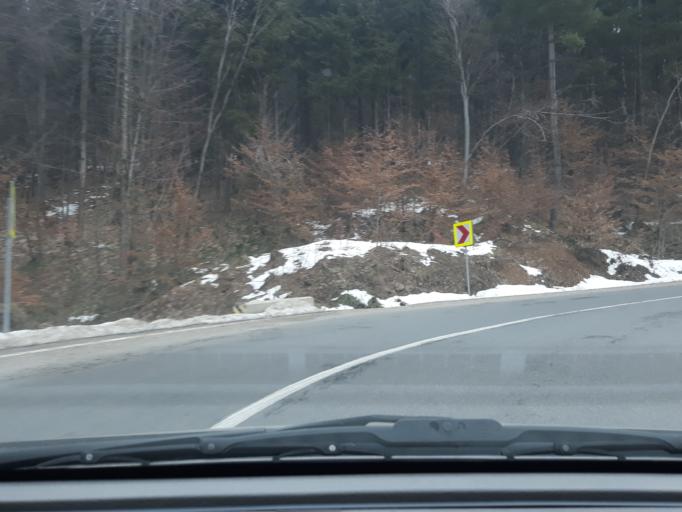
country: RO
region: Bihor
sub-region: Oras Alesd
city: Padurea Neagra
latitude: 47.1296
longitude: 22.4243
